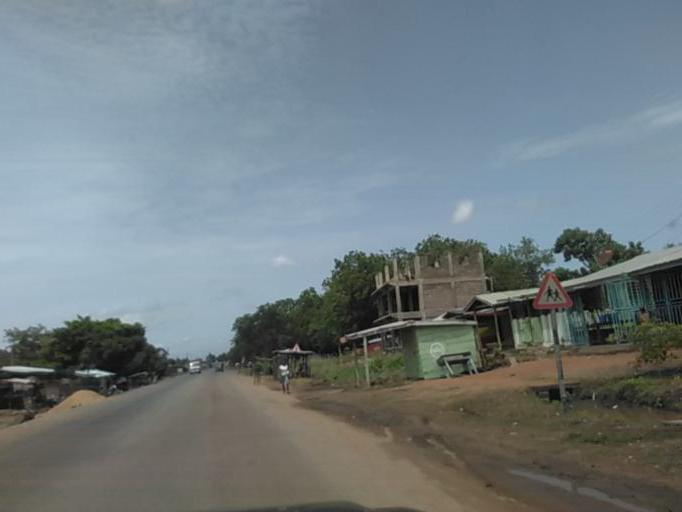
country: GH
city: Akropong
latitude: 6.1636
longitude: 0.0649
